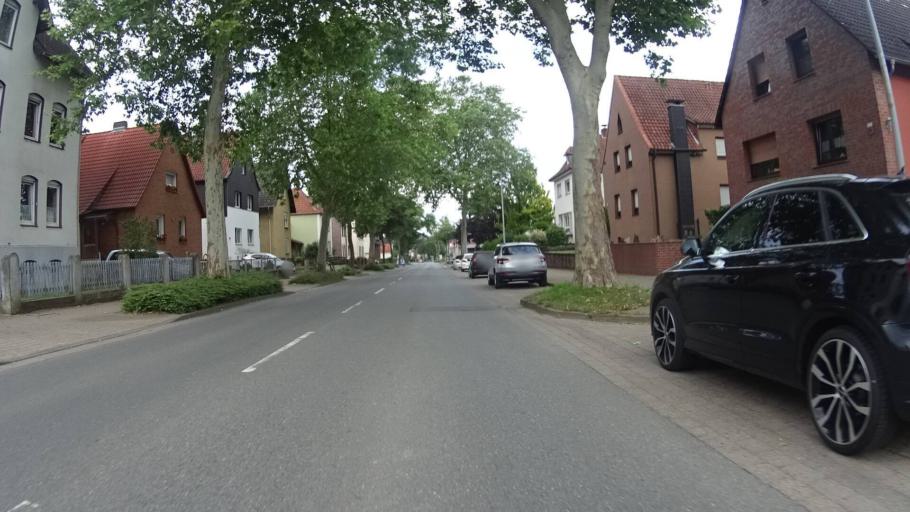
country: DE
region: Lower Saxony
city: Holzminden
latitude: 51.8278
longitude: 9.4733
